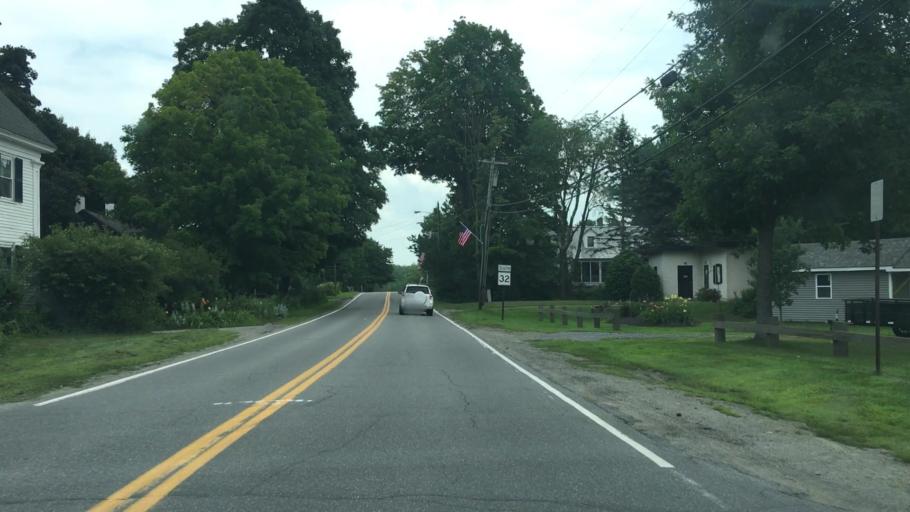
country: US
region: Maine
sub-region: Kennebec County
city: Vassalboro
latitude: 44.4477
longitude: -69.6065
